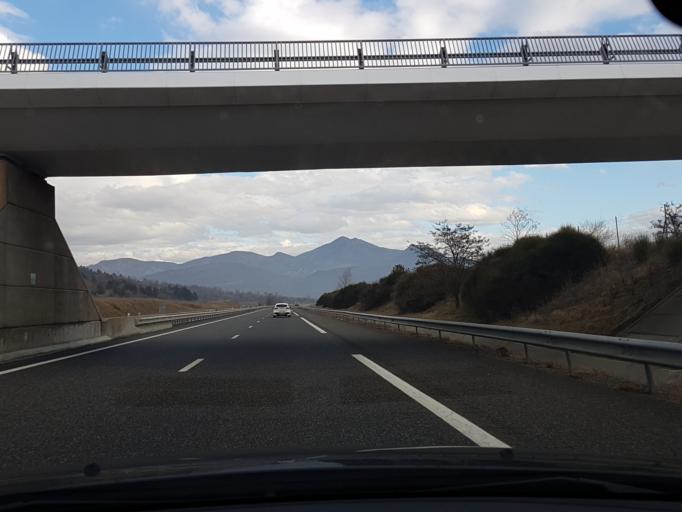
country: FR
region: Provence-Alpes-Cote d'Azur
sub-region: Departement des Hautes-Alpes
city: Tallard
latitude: 44.3931
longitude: 5.9426
